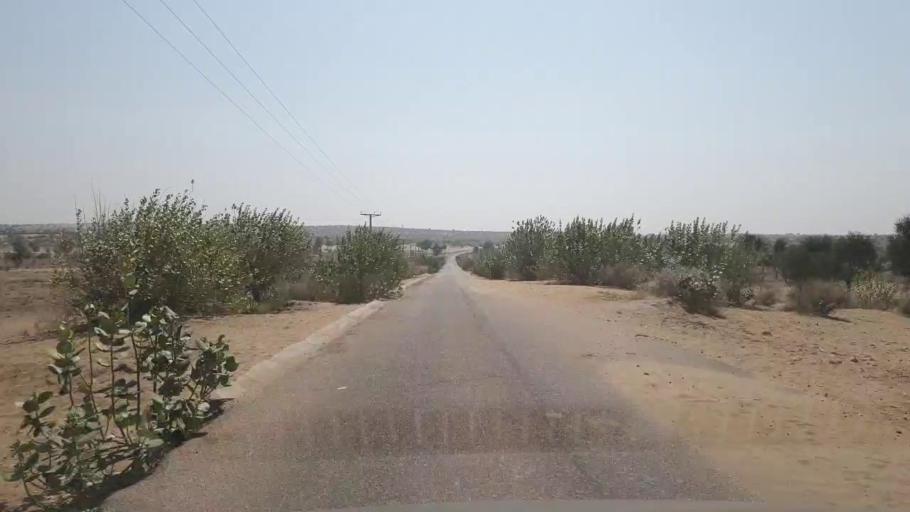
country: PK
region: Sindh
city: Chor
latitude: 25.6443
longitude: 70.1706
